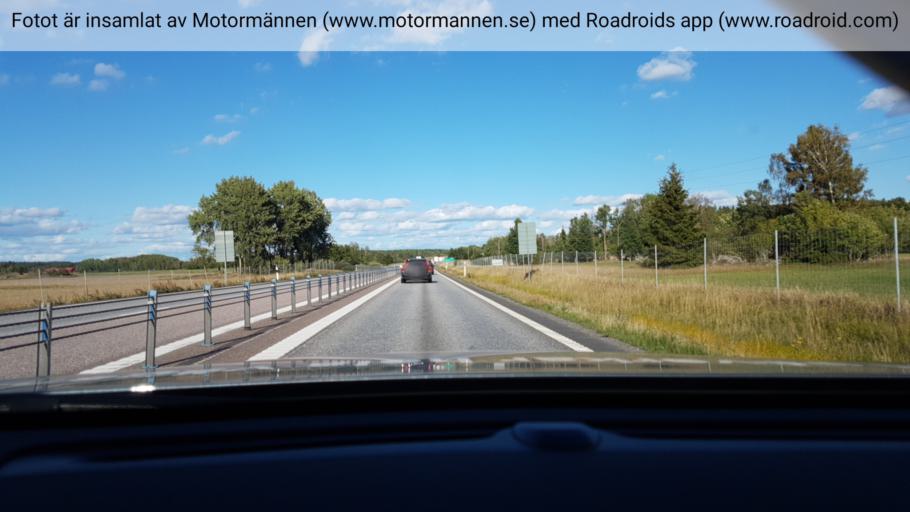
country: SE
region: Vaestmanland
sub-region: Kopings Kommun
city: Koping
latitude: 59.5642
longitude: 16.0734
